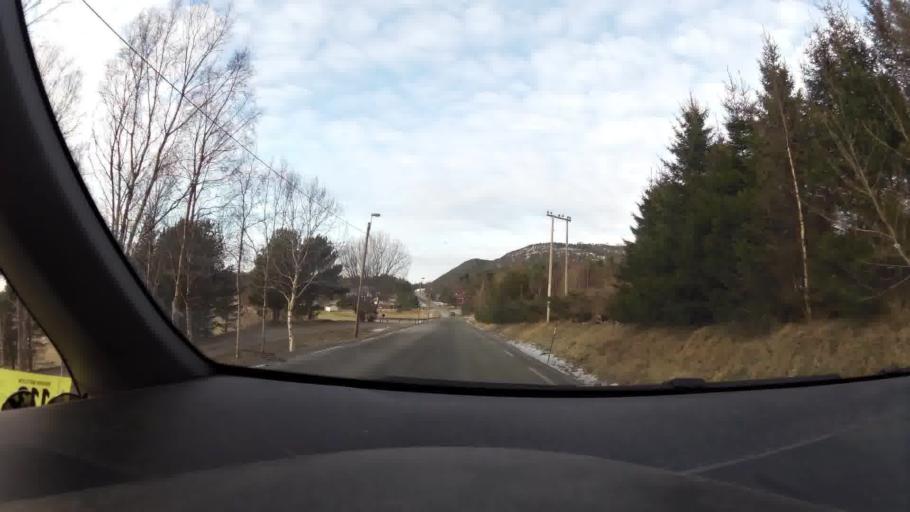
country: NO
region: More og Romsdal
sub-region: Kristiansund
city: Rensvik
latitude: 63.0887
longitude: 7.8554
